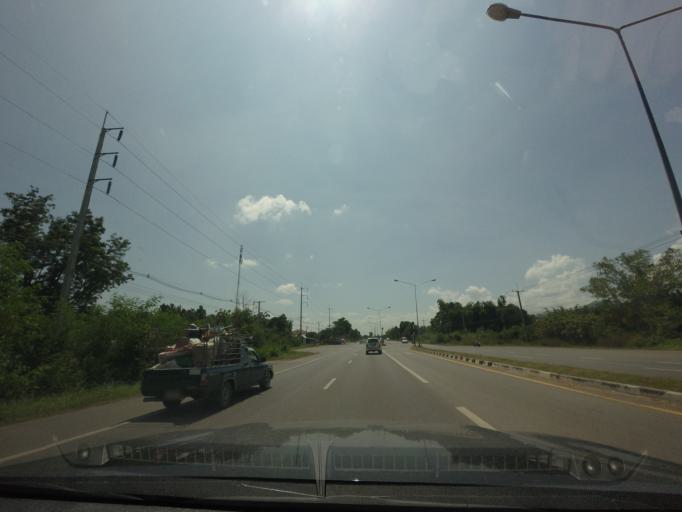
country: TH
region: Phetchabun
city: Lom Sak
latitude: 16.6702
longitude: 101.1595
